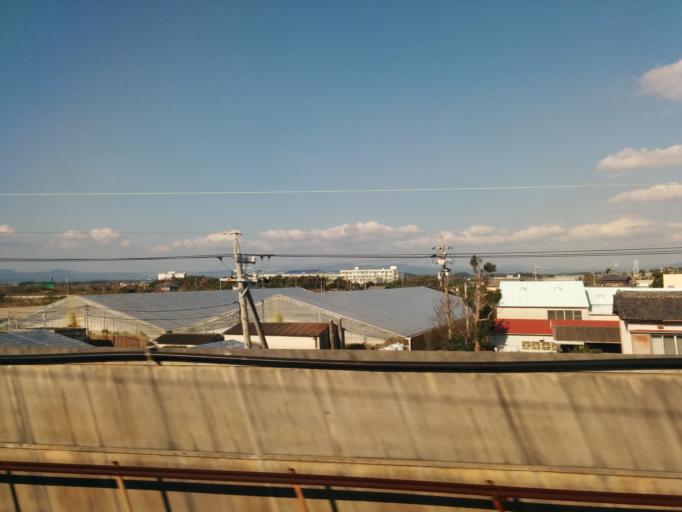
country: JP
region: Shizuoka
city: Kosai-shi
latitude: 34.6871
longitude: 137.6281
